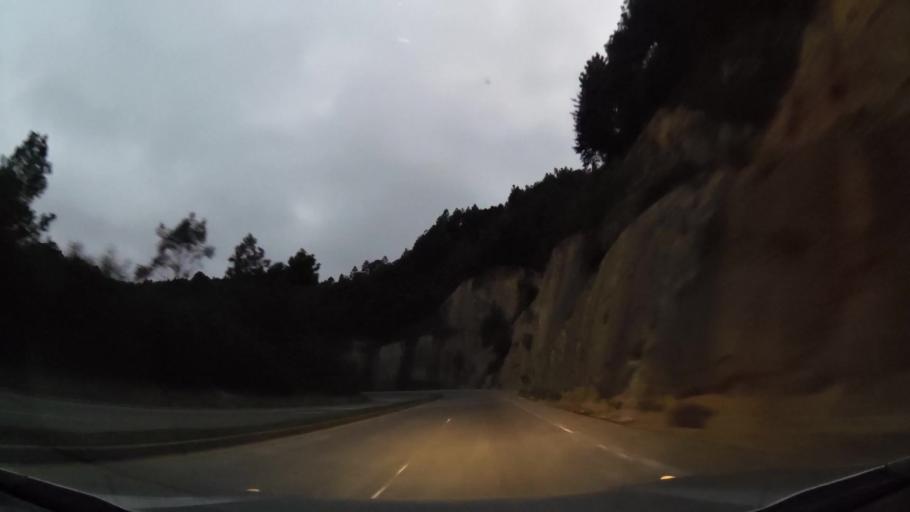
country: GT
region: Chimaltenango
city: Santa Apolonia
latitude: 14.8212
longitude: -91.0053
